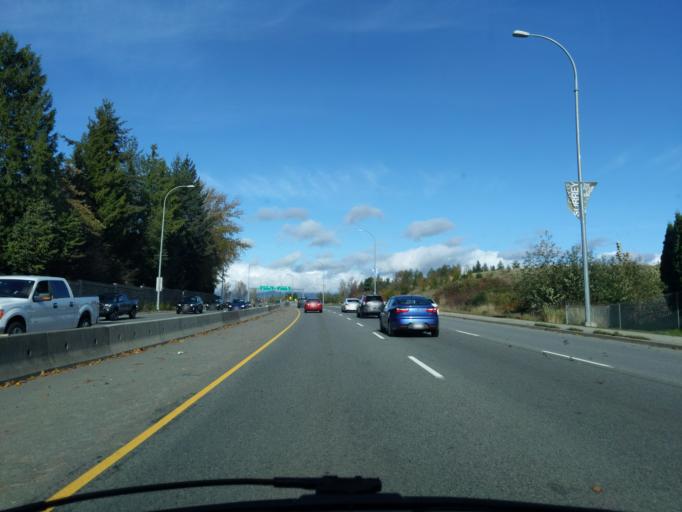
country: CA
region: British Columbia
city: Surrey
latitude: 49.1985
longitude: -122.7994
